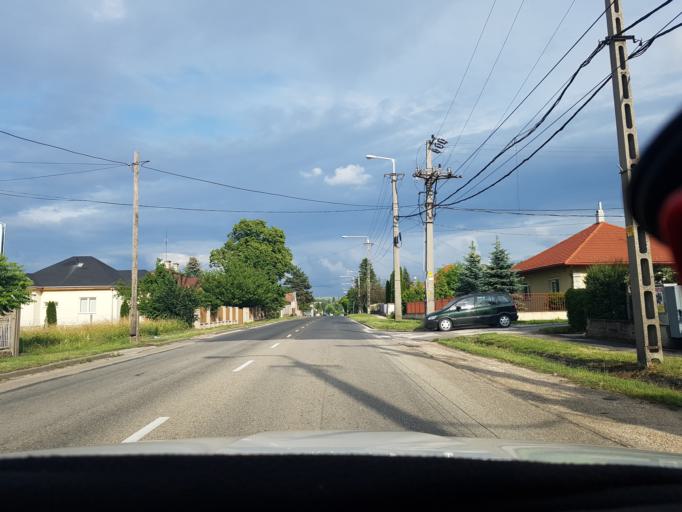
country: HU
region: Komarom-Esztergom
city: Labatlan
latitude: 47.7529
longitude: 18.4732
